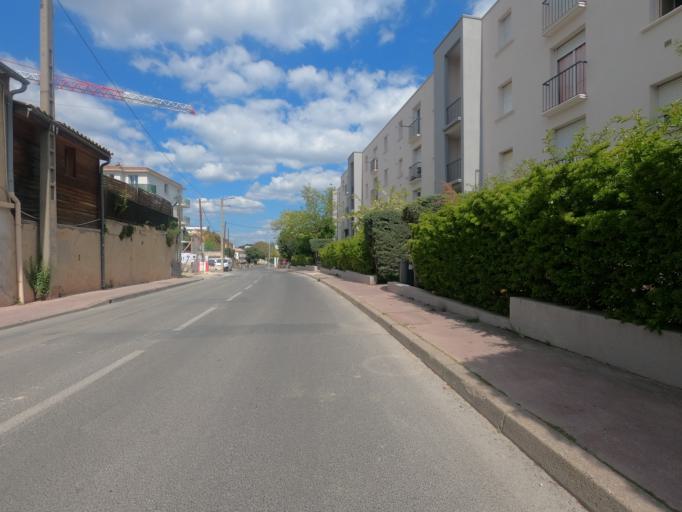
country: FR
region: Languedoc-Roussillon
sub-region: Departement de l'Herault
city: Montpellier
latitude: 43.5903
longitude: 3.8722
